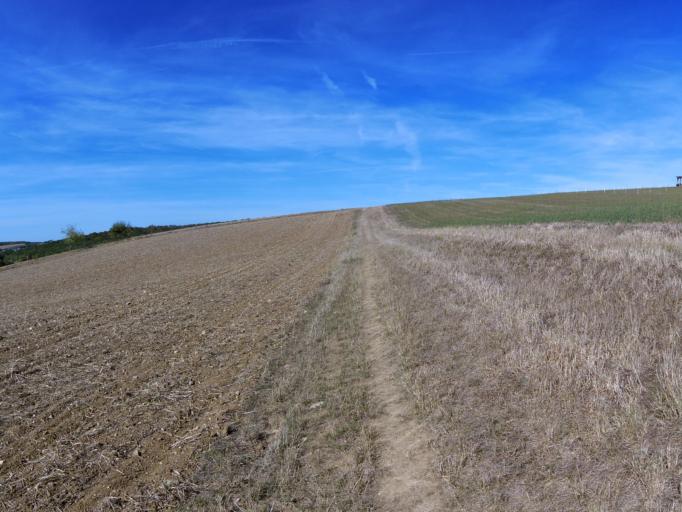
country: DE
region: Bavaria
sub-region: Regierungsbezirk Unterfranken
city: Eisingen
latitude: 49.7656
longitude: 9.8226
